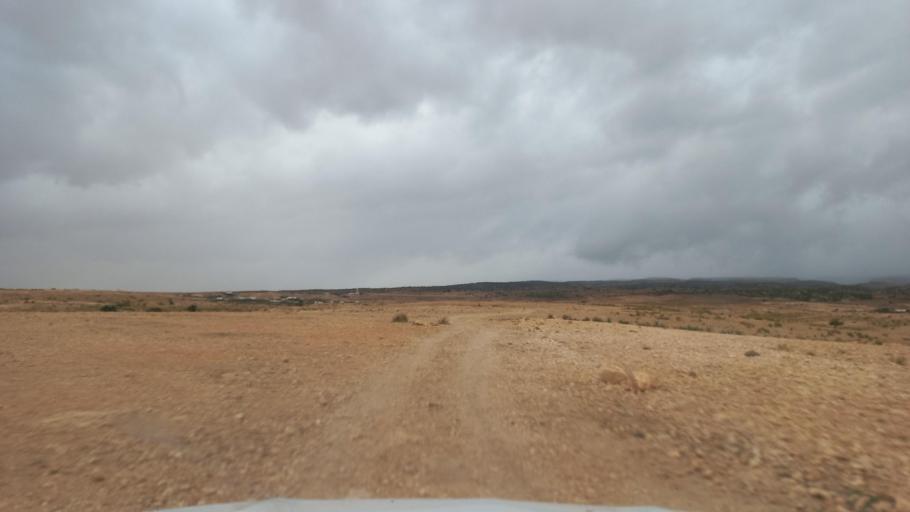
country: TN
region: Al Qasrayn
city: Kasserine
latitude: 35.2780
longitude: 8.9364
